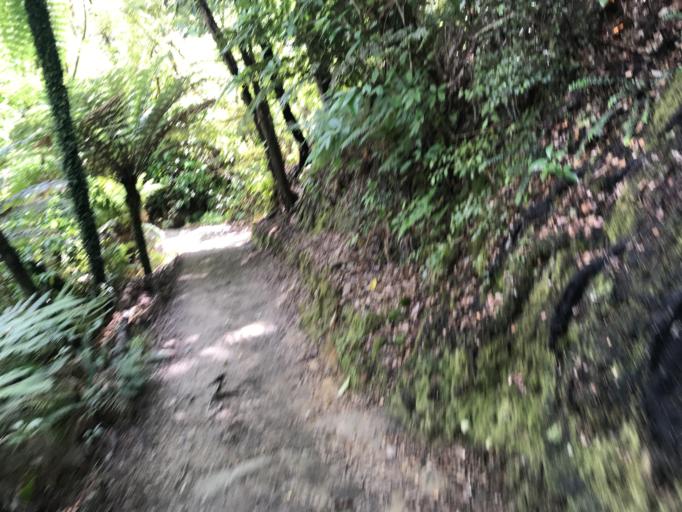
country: NZ
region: Marlborough
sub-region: Marlborough District
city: Picton
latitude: -41.2597
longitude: 173.9332
